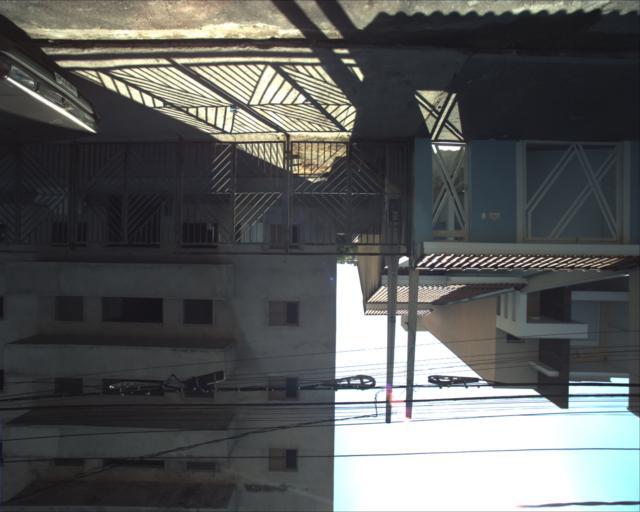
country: BR
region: Sao Paulo
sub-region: Sorocaba
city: Sorocaba
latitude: -23.5085
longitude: -47.4268
